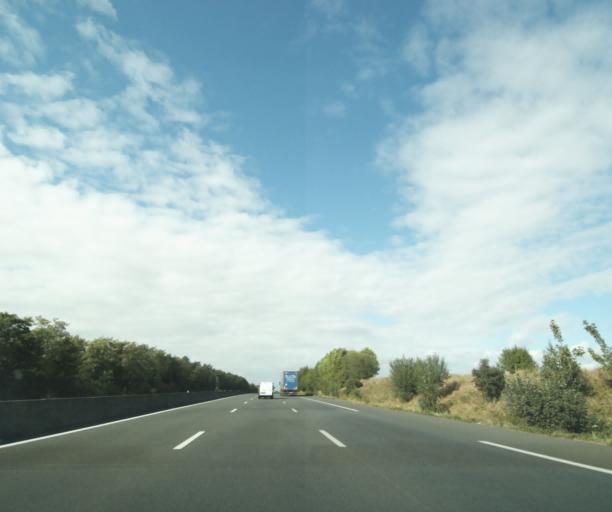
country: FR
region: Centre
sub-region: Departement d'Eure-et-Loir
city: Janville
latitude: 48.1657
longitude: 1.8538
